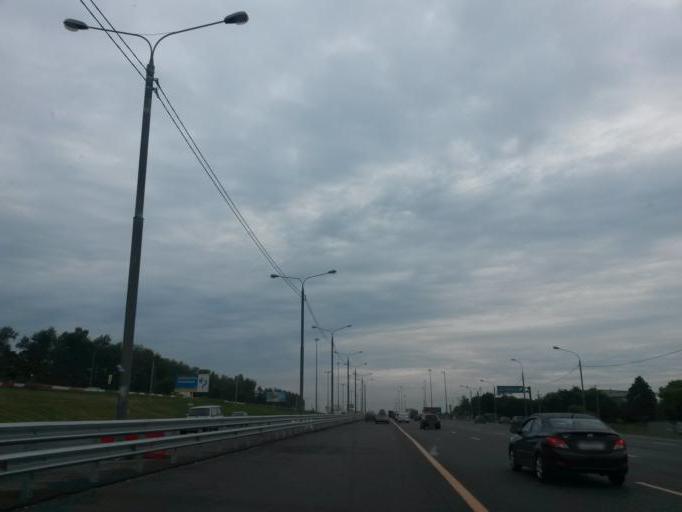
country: RU
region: Moskovskaya
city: Shcherbinka
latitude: 55.4741
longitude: 37.6164
